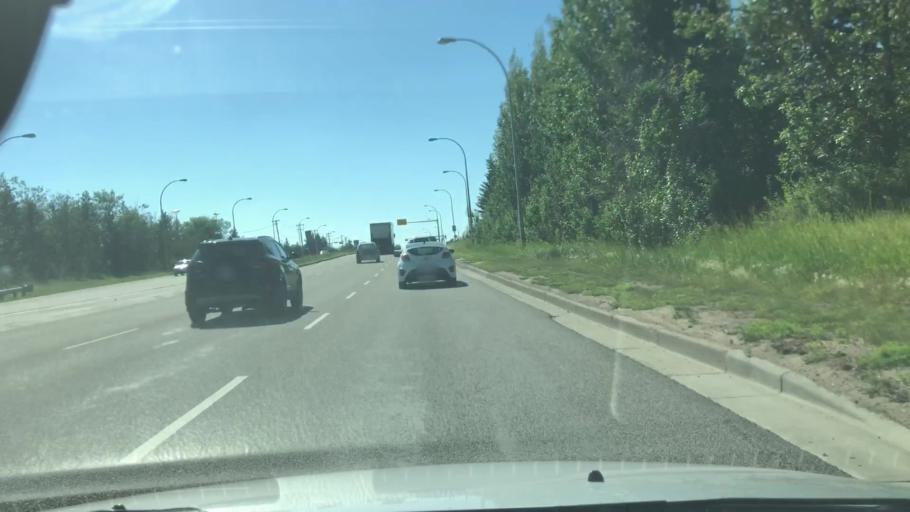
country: CA
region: Alberta
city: Edmonton
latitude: 53.5801
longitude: -113.5305
